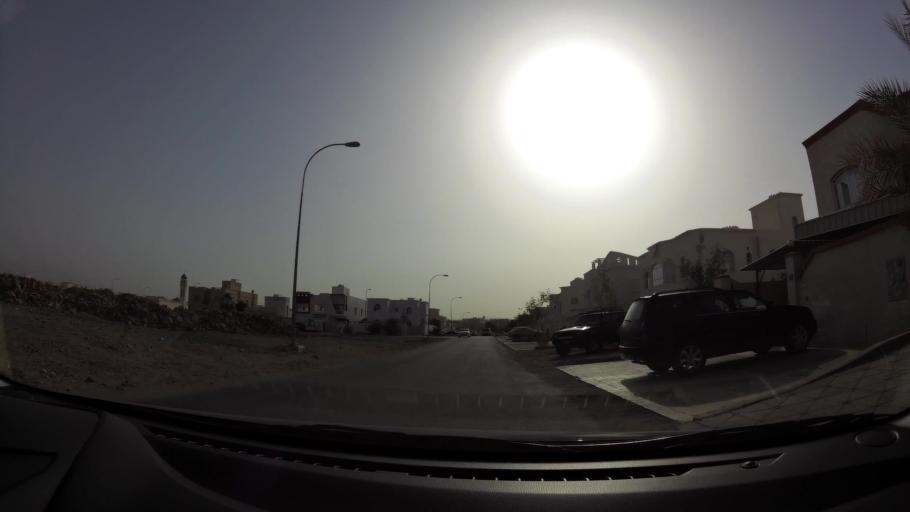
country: OM
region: Muhafazat Masqat
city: Bawshar
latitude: 23.5430
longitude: 58.3621
